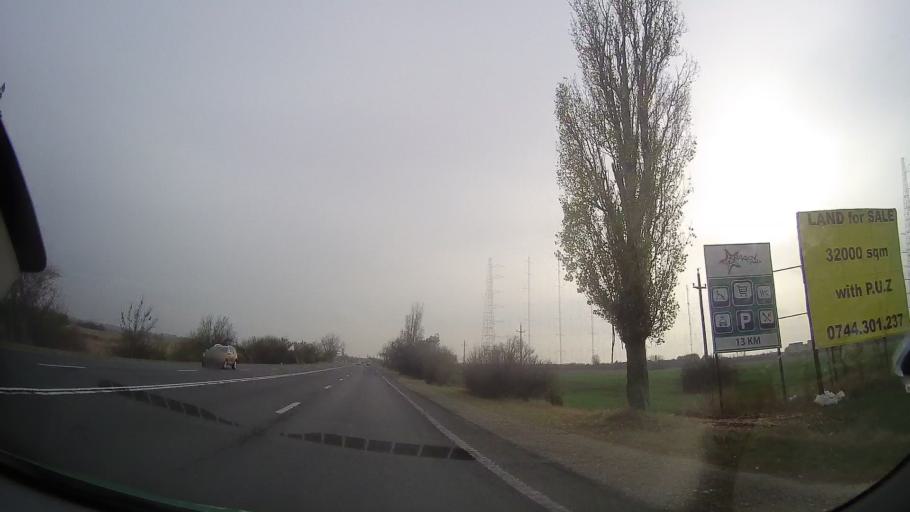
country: RO
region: Ilfov
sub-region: Comuna Ciolpani
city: Ciolpani
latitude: 44.7525
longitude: 26.1068
